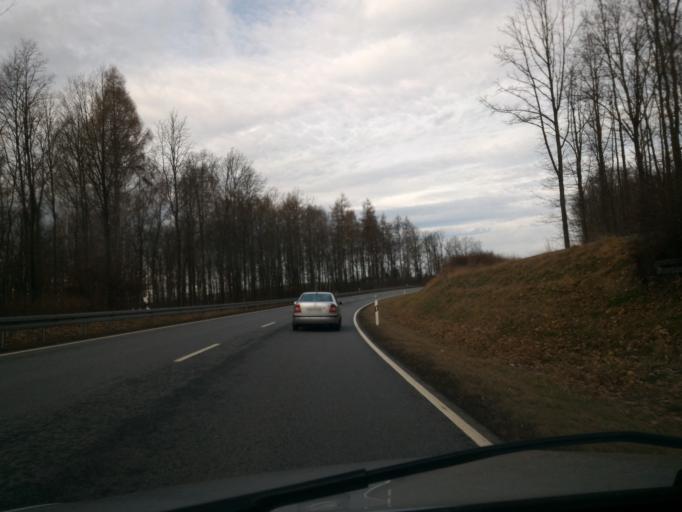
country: DE
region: Saxony
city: Bischofswerda
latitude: 51.1094
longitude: 14.1804
